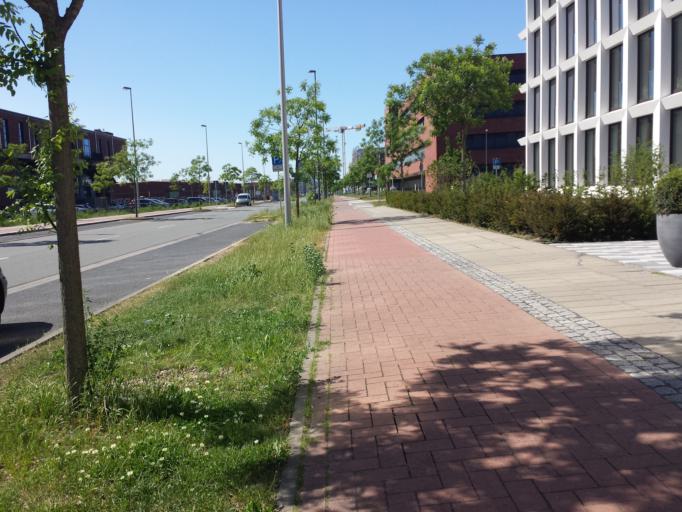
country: DE
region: Bremen
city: Bremen
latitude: 53.0911
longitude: 8.7747
